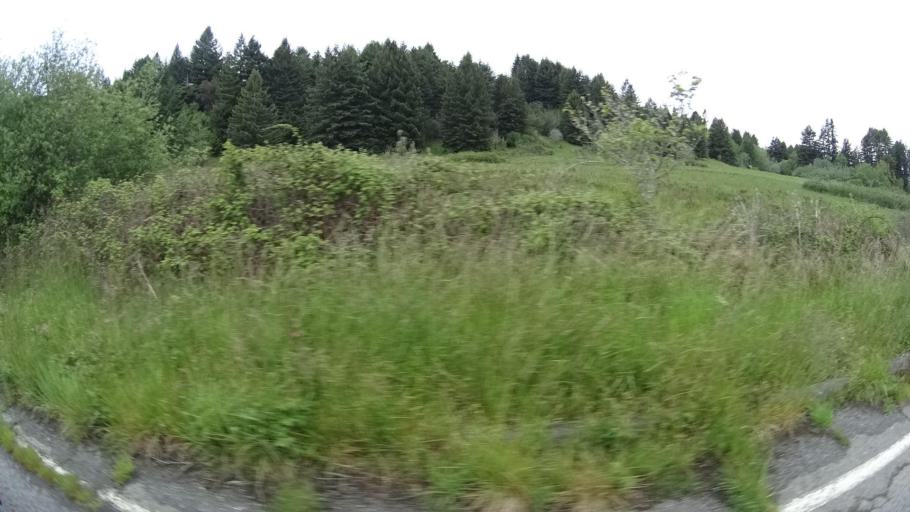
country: US
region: California
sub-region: Humboldt County
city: Blue Lake
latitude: 40.8603
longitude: -123.9956
